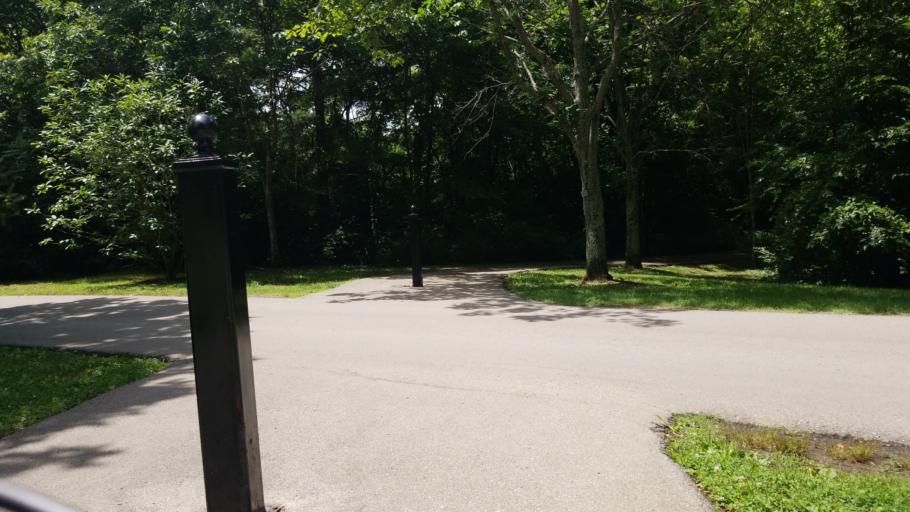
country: US
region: Tennessee
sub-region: Davidson County
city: Forest Hills
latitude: 36.0362
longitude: -86.8421
